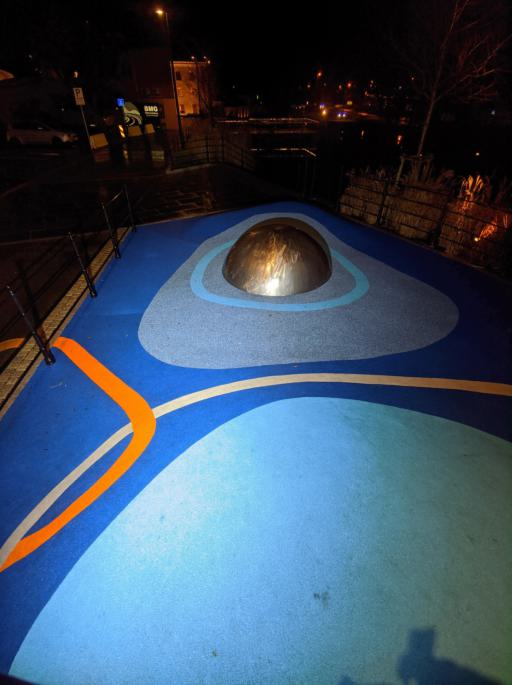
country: NO
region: Rogaland
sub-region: Time
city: Bryne
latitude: 58.7364
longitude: 5.6440
